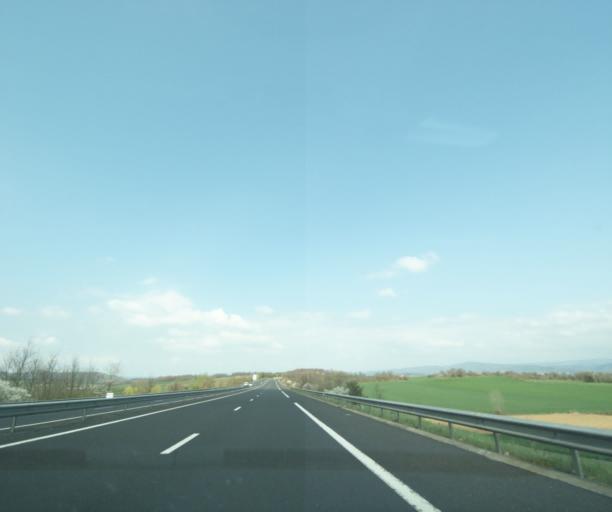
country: FR
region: Auvergne
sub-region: Departement de la Haute-Loire
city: Lempdes-sur-Allagnon
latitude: 45.3491
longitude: 3.2774
